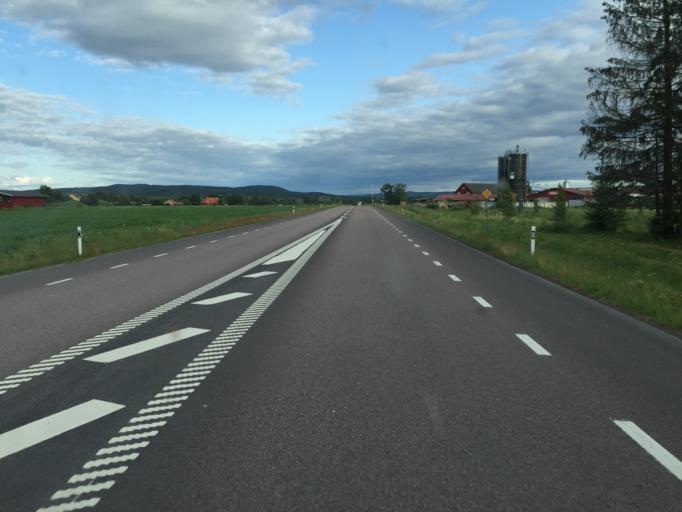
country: SE
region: Dalarna
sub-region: Gagnefs Kommun
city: Gagnef
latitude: 60.5898
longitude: 15.0872
